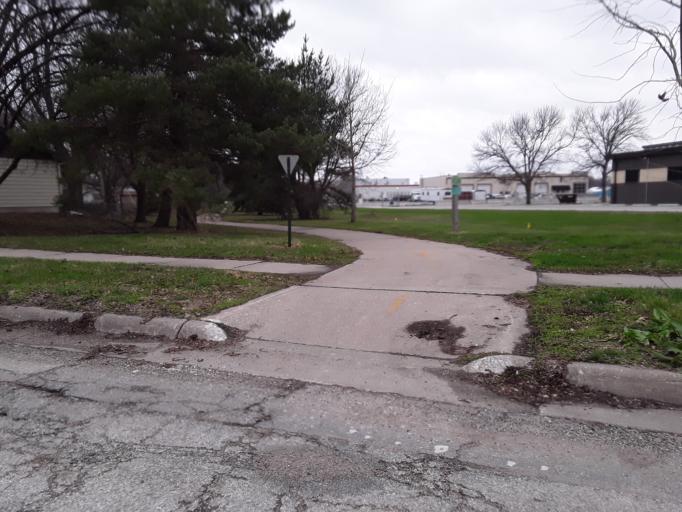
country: US
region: Nebraska
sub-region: Lancaster County
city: Lincoln
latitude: 40.8466
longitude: -96.6588
